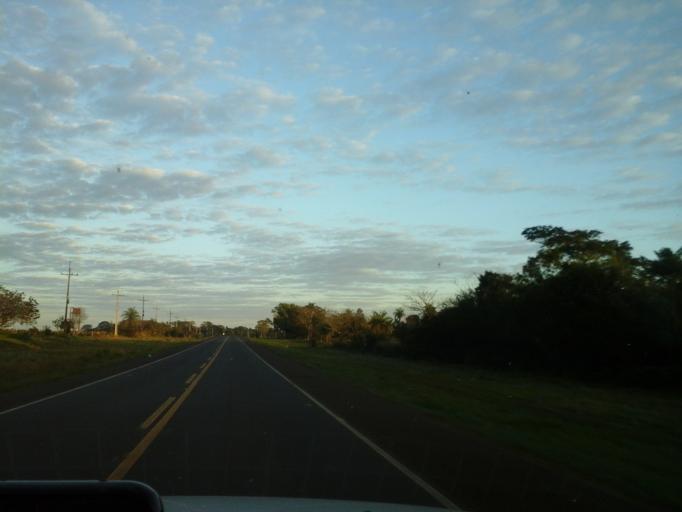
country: PY
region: Misiones
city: San Patricio
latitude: -27.0252
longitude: -56.7043
